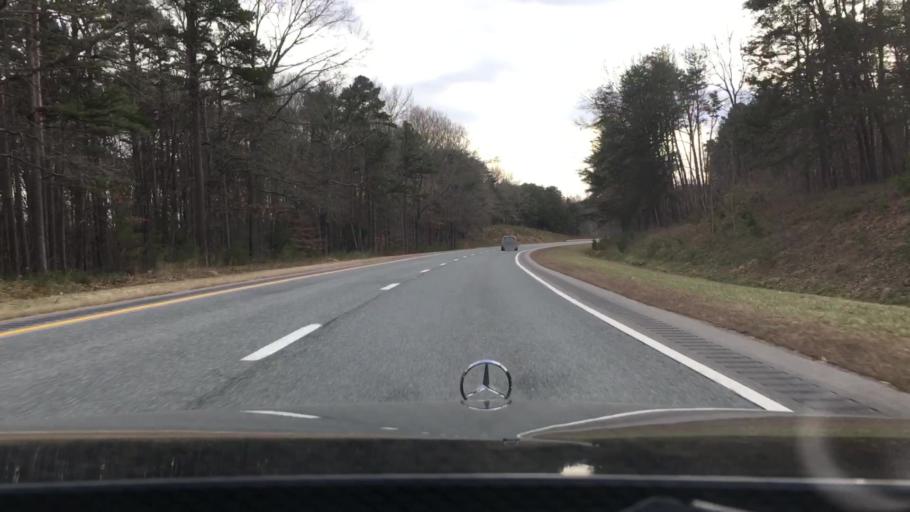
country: US
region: Virginia
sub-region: Pittsylvania County
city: Gretna
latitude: 36.9299
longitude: -79.3761
